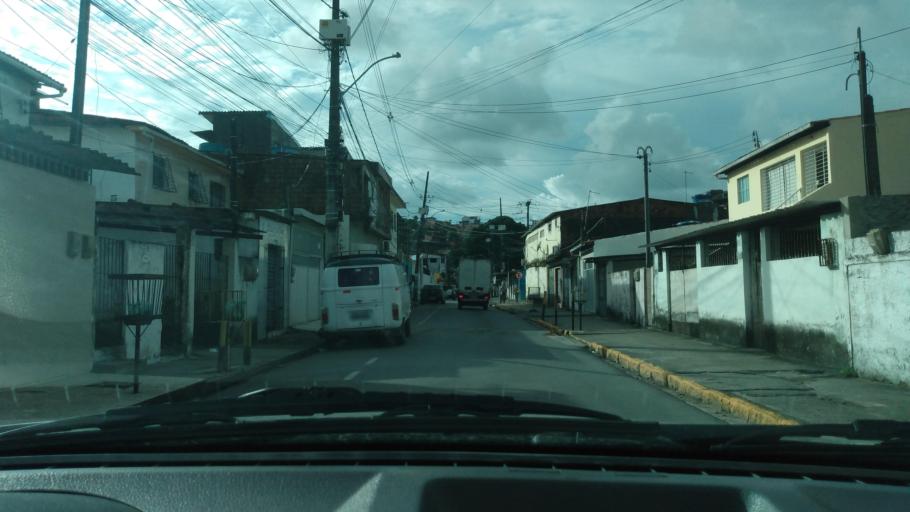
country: BR
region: Pernambuco
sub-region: Jaboatao Dos Guararapes
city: Jaboatao dos Guararapes
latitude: -8.1290
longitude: -34.9380
